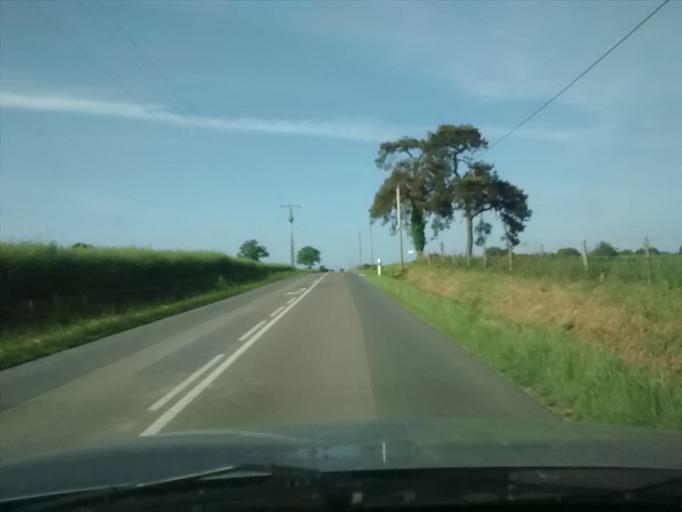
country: FR
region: Pays de la Loire
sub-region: Departement de la Mayenne
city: Meslay-du-Maine
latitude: 47.9998
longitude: -0.5986
